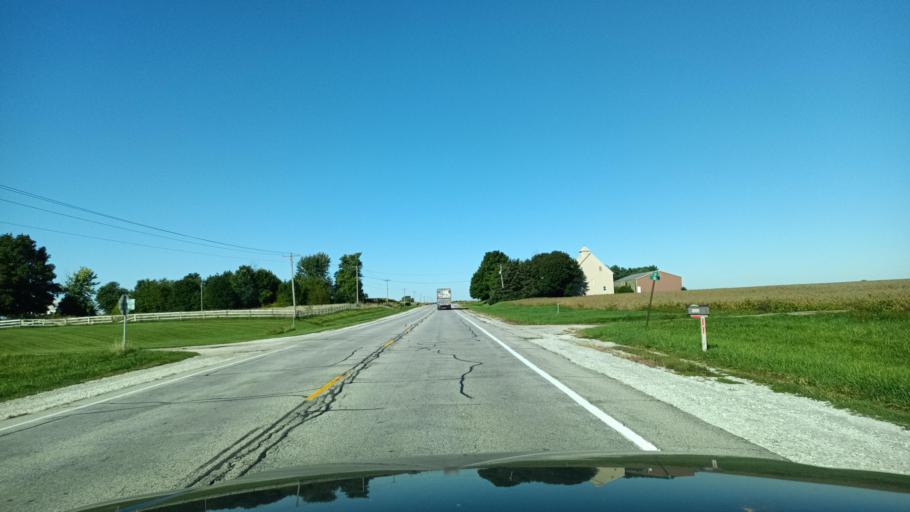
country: US
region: Illinois
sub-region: Warren County
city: Monmouth
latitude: 40.8785
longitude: -90.7100
